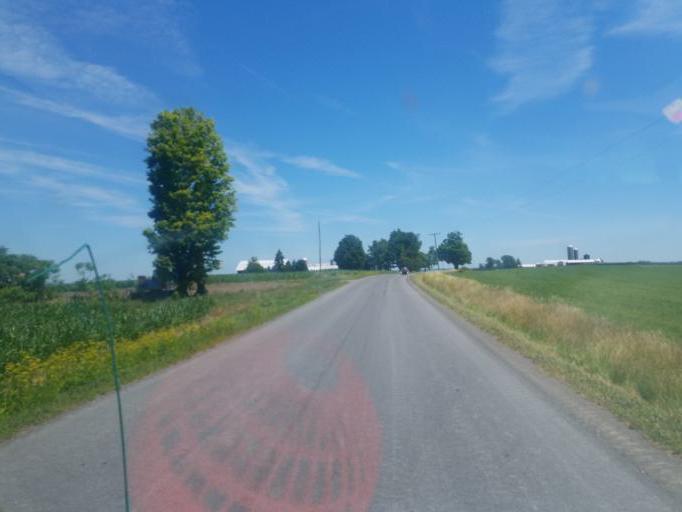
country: US
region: New York
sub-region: Yates County
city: Penn Yan
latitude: 42.6329
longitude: -77.0139
